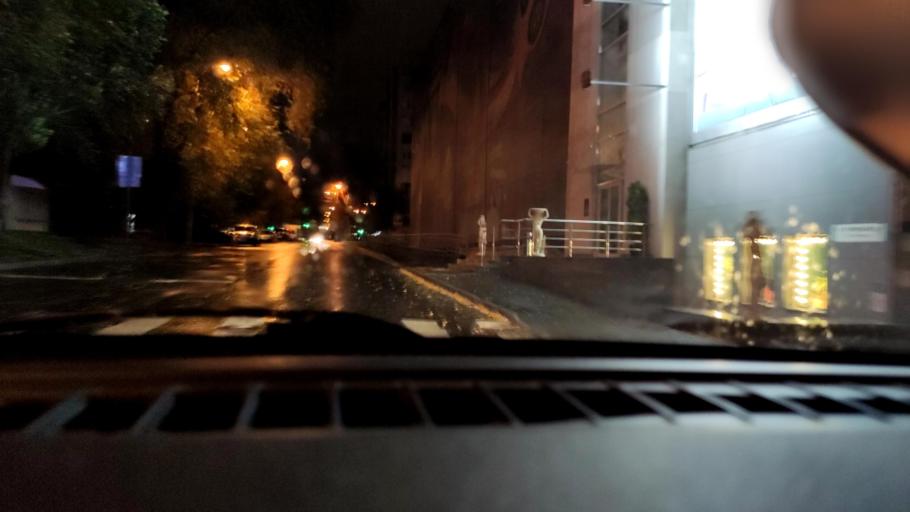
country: RU
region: Samara
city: Samara
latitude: 53.2063
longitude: 50.1274
